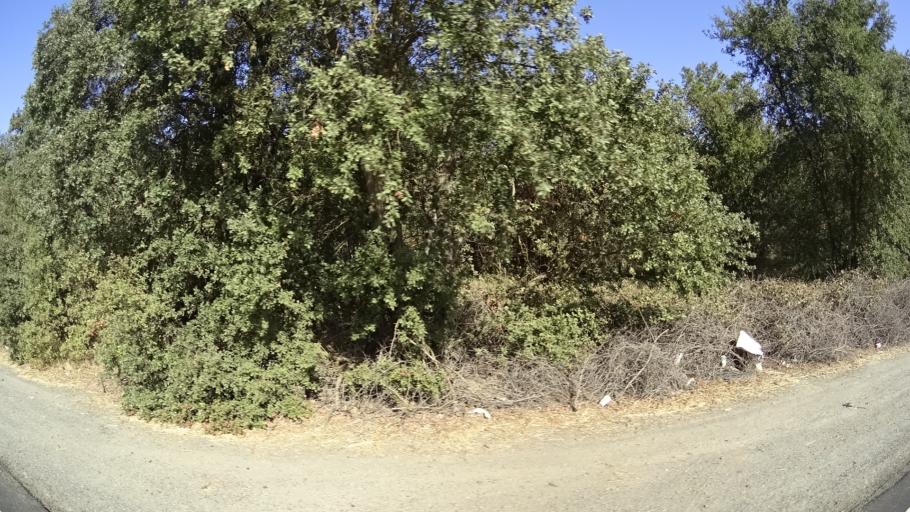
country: US
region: California
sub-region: Yolo County
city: West Sacramento
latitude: 38.6750
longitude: -121.6325
